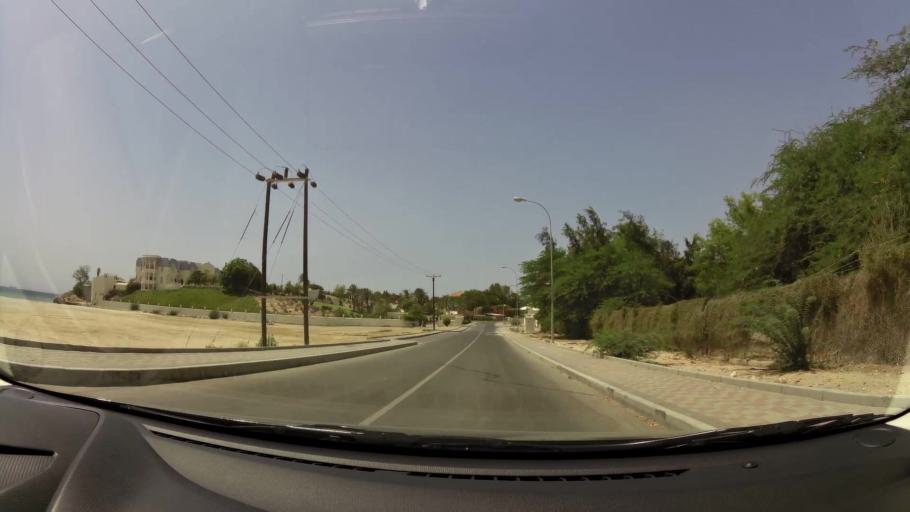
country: OM
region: Muhafazat Masqat
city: Muscat
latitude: 23.6339
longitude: 58.4879
